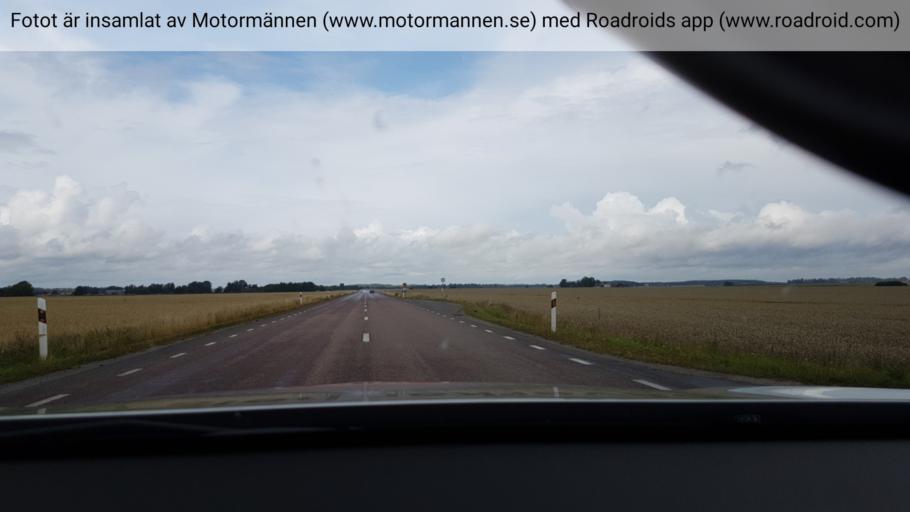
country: SE
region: Uppsala
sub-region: Uppsala Kommun
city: Gamla Uppsala
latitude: 59.9000
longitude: 17.5460
